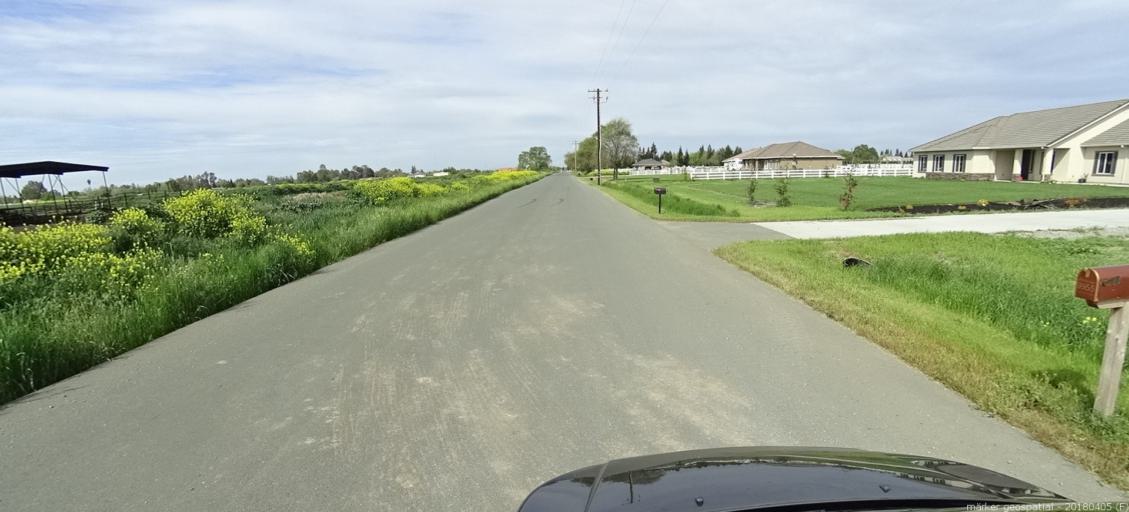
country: US
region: California
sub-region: Sacramento County
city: Galt
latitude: 38.2728
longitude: -121.3266
